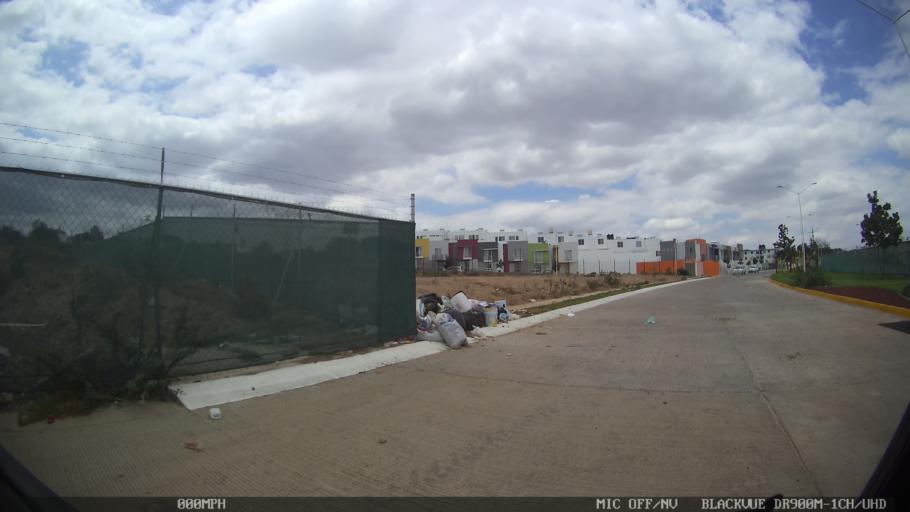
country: MX
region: Jalisco
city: Tonala
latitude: 20.6344
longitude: -103.2559
